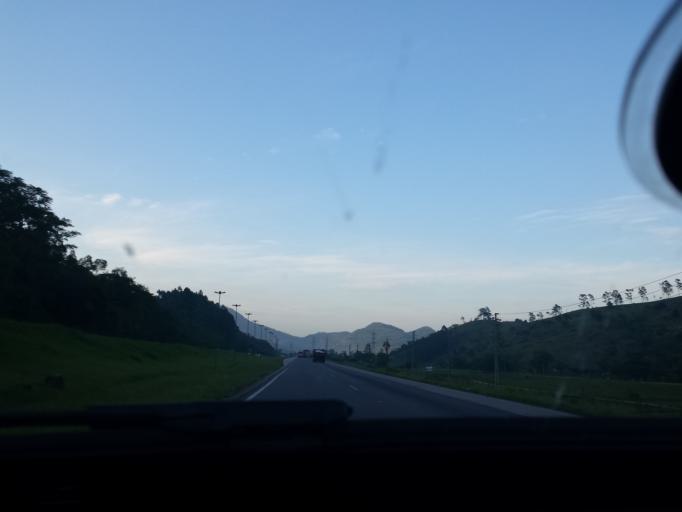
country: BR
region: Santa Catarina
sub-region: Imbituba
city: Imbituba
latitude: -28.0297
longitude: -48.7057
